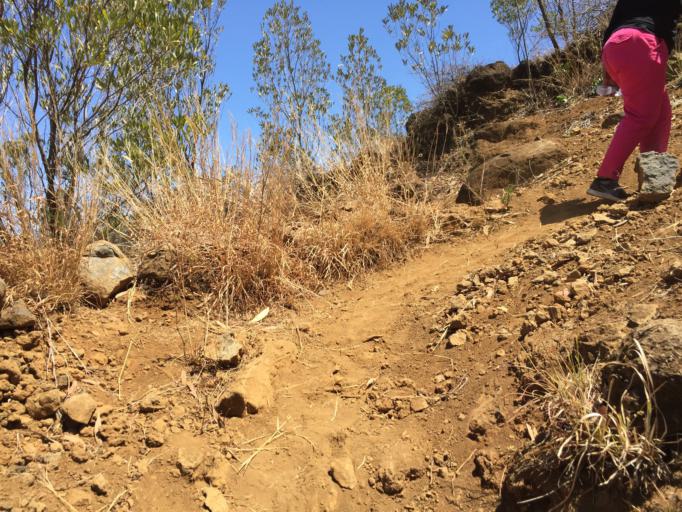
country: CV
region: Mosteiros
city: Porto dos Mosteiros
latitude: 15.0084
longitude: -24.3823
